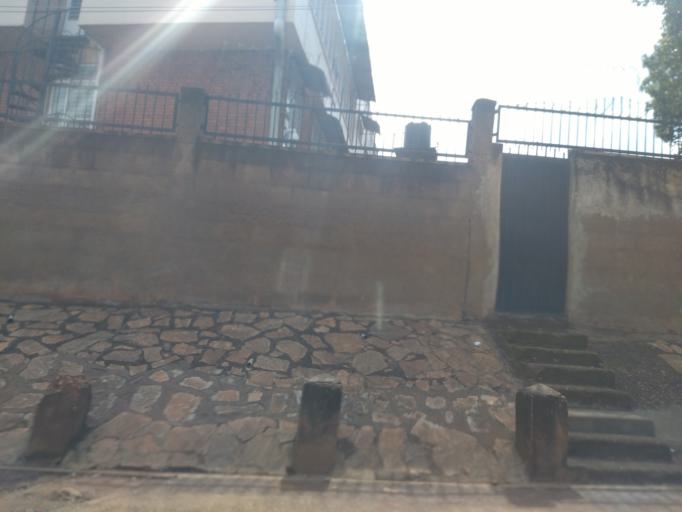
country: UG
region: Central Region
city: Kampala Central Division
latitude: 0.3309
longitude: 32.5747
